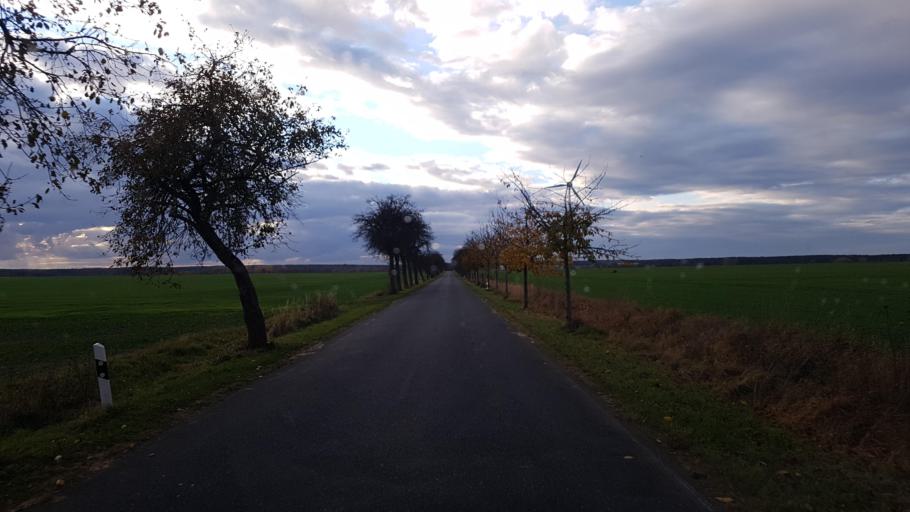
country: DE
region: Saxony-Anhalt
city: Zahna
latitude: 51.9455
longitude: 12.8107
